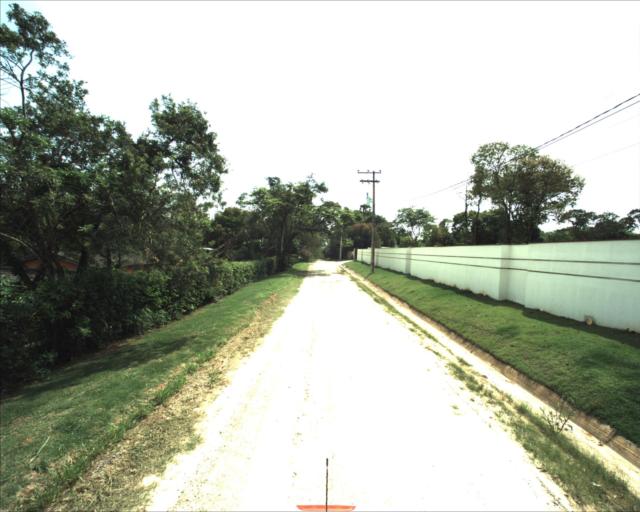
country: BR
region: Sao Paulo
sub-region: Salto De Pirapora
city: Salto de Pirapora
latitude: -23.5656
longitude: -47.5376
